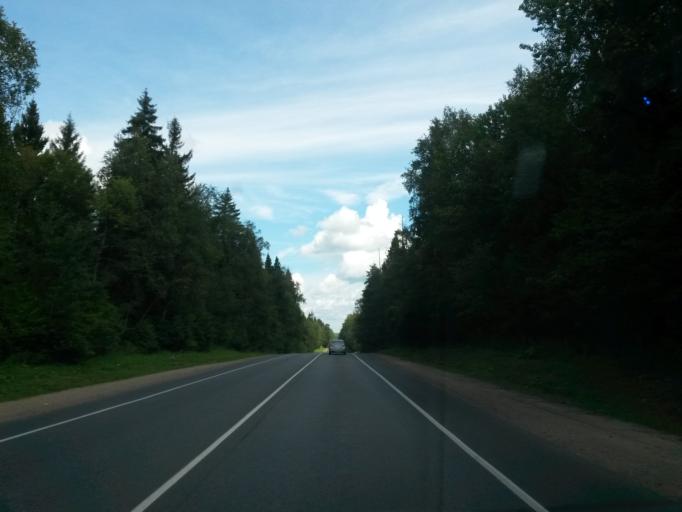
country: RU
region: Jaroslavl
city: Pereslavl'-Zalesskiy
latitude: 56.8073
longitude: 38.8975
